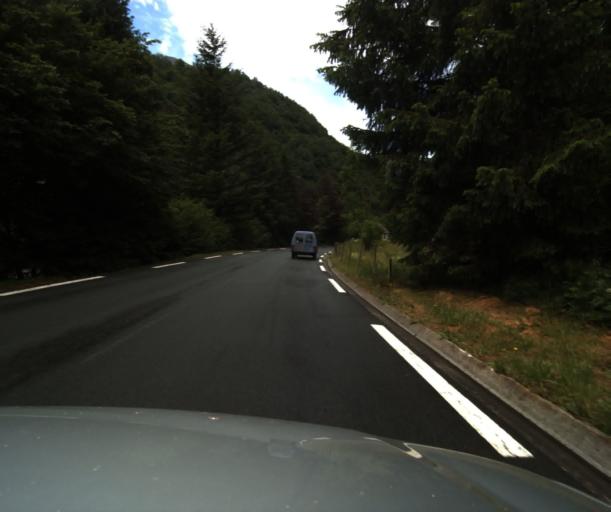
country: FR
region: Midi-Pyrenees
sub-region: Departement des Hautes-Pyrenees
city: Luz-Saint-Sauveur
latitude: 42.8003
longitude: 0.0139
